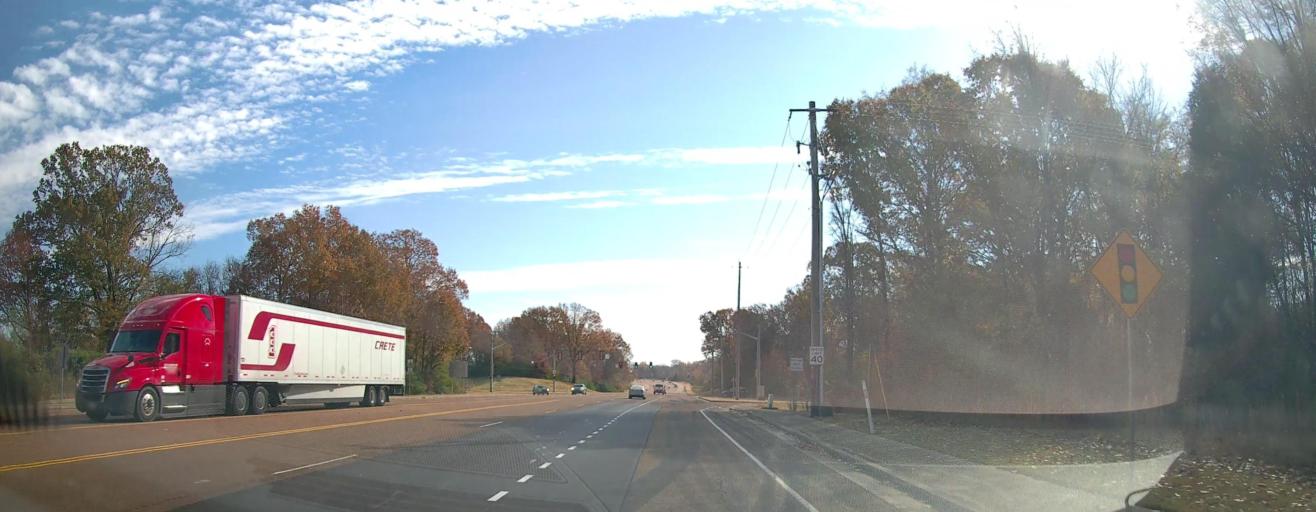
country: US
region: Tennessee
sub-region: Shelby County
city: Collierville
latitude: 35.0221
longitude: -89.6571
